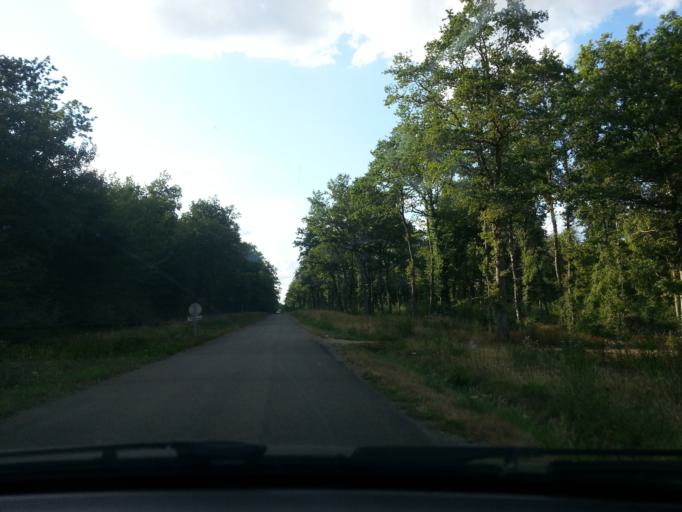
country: FR
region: Bourgogne
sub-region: Departement de Saone-et-Loire
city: Dracy-le-Fort
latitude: 46.7664
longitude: 4.7711
